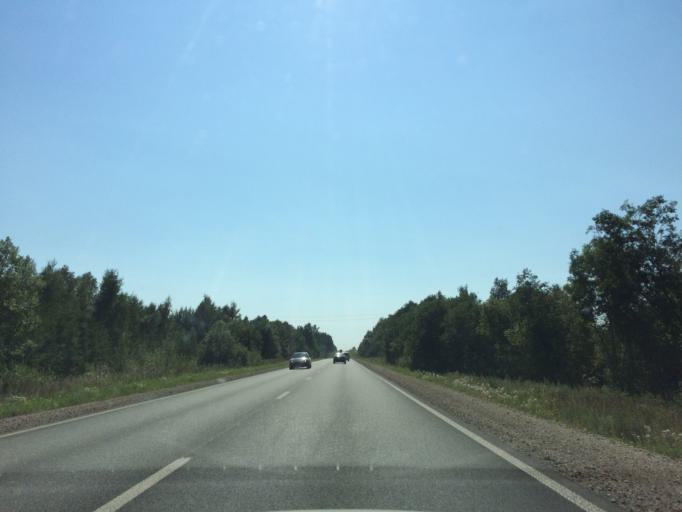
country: LV
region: Rezekne
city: Rezekne
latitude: 56.3874
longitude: 27.2081
